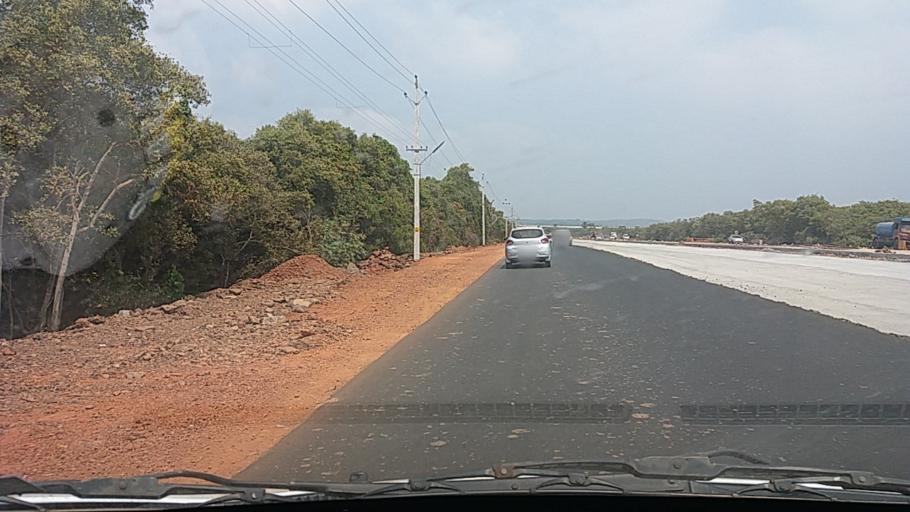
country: IN
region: Goa
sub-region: North Goa
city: Taleigao
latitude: 15.4858
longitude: 73.8464
